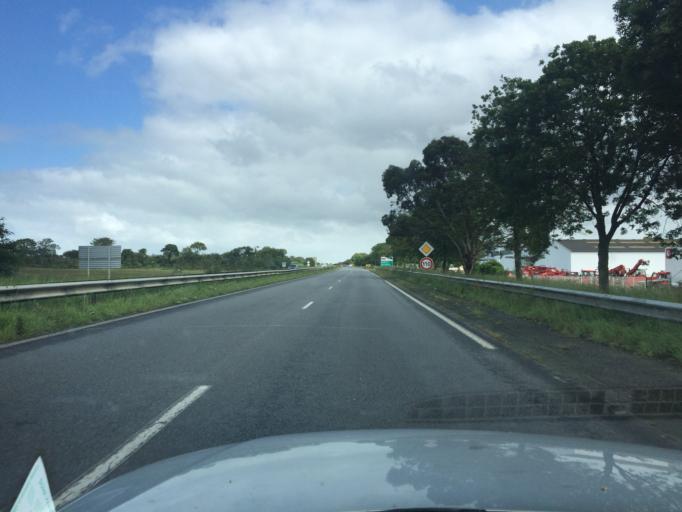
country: FR
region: Brittany
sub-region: Departement du Finistere
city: Gouesnou
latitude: 48.4331
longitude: -4.4589
